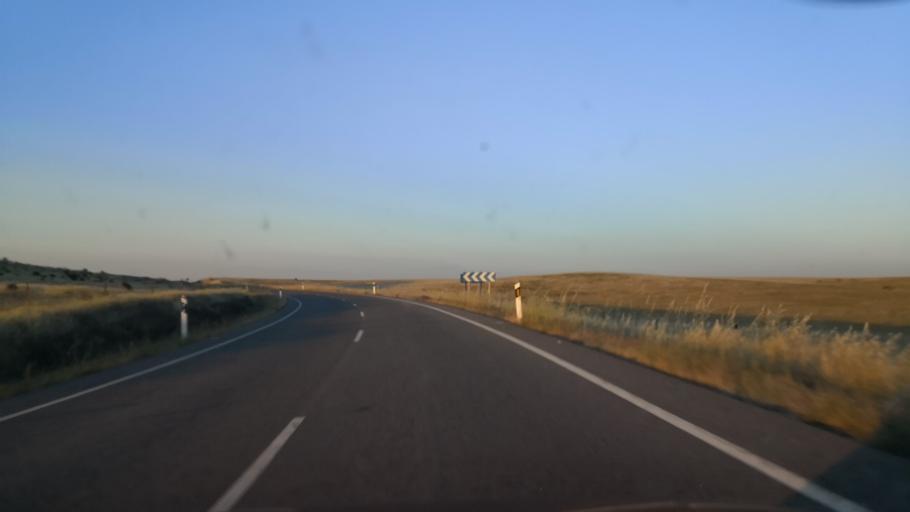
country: ES
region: Extremadura
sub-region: Provincia de Caceres
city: Alcantara
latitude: 39.6165
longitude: -6.9433
